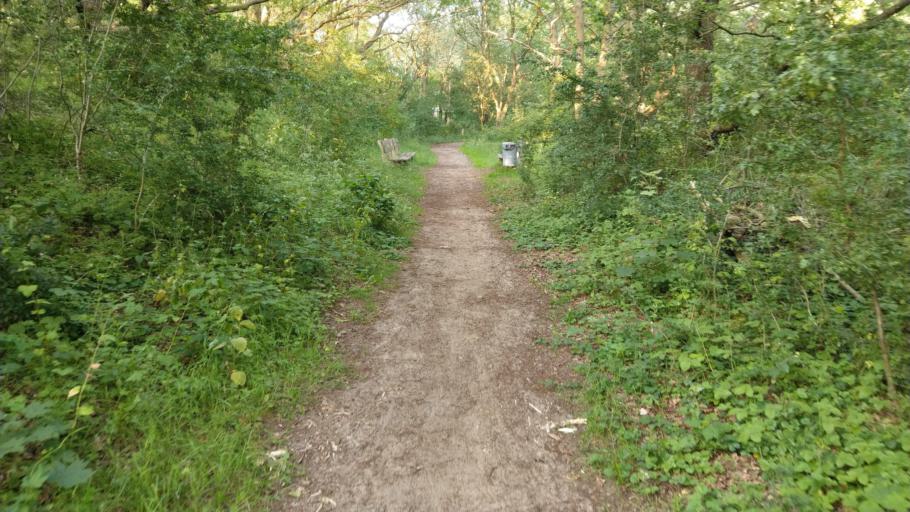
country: NL
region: North Holland
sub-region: Gemeente Castricum
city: Castricum
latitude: 52.5556
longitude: 4.6409
